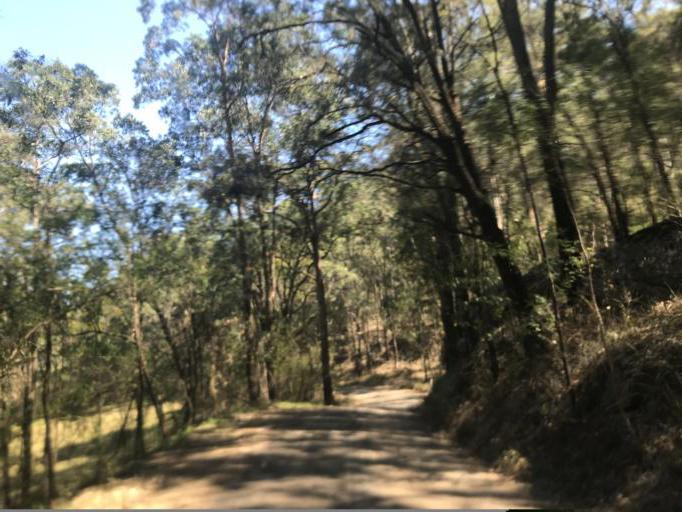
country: AU
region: New South Wales
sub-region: Wyong Shire
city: Little Jilliby
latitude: -33.1963
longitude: 151.0080
